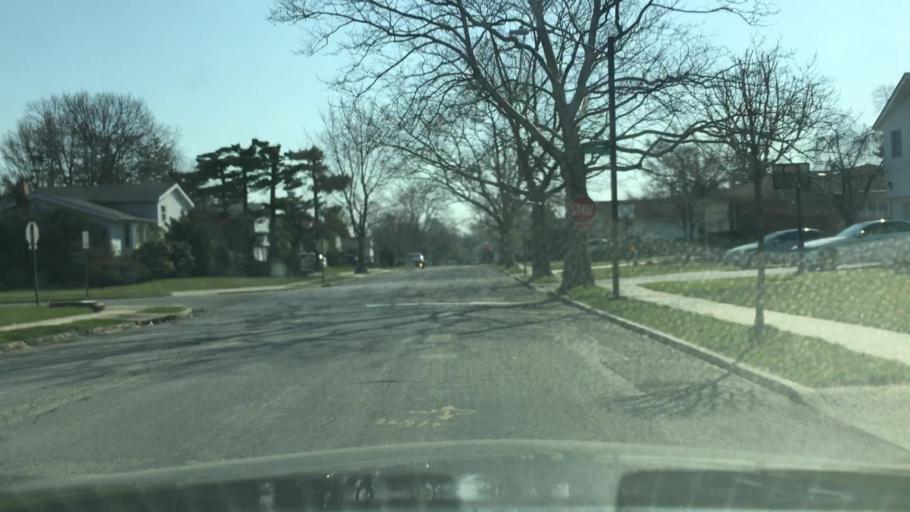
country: US
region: New York
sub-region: Nassau County
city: Jericho
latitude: 40.7799
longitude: -73.5438
